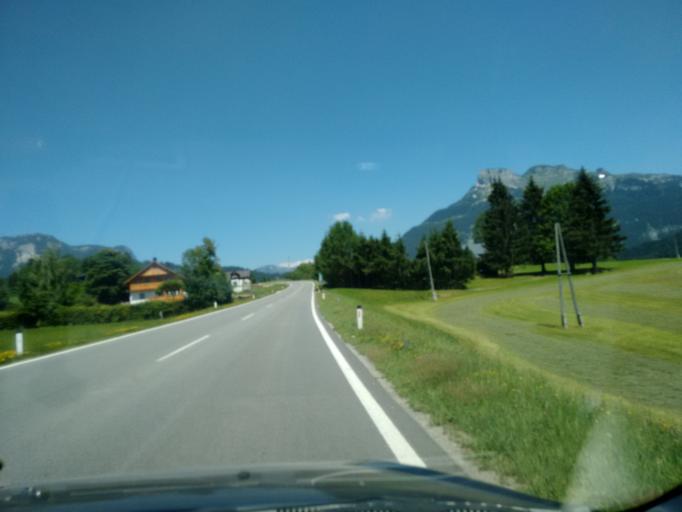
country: AT
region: Styria
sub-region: Politischer Bezirk Liezen
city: Bad Aussee
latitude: 47.6154
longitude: 13.7630
